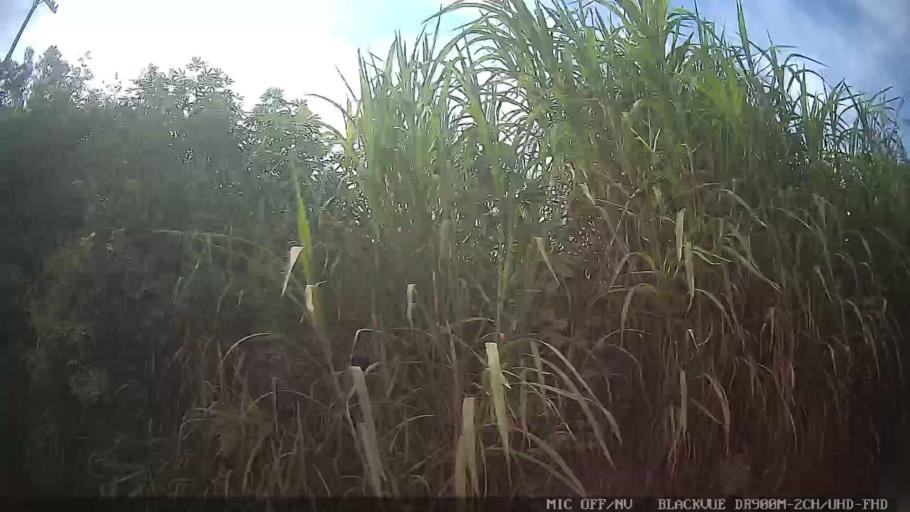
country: BR
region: Sao Paulo
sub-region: Braganca Paulista
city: Braganca Paulista
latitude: -22.9877
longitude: -46.6484
